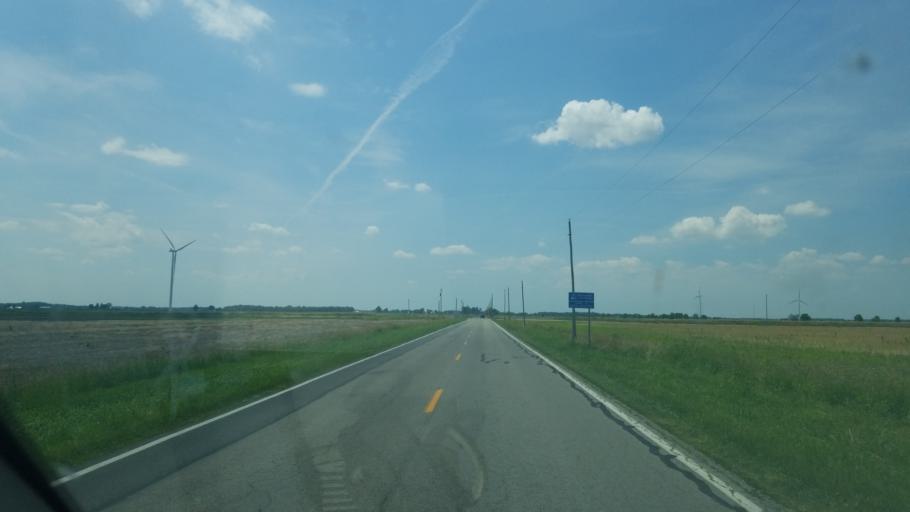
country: US
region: Ohio
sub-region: Hardin County
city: Ada
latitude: 40.7763
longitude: -83.7257
